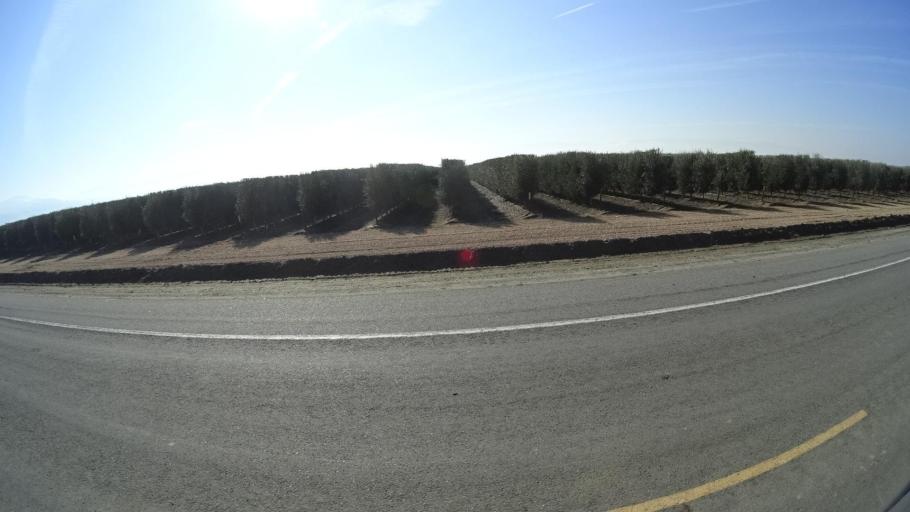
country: US
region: California
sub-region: Kern County
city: Weedpatch
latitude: 35.1942
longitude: -118.8895
